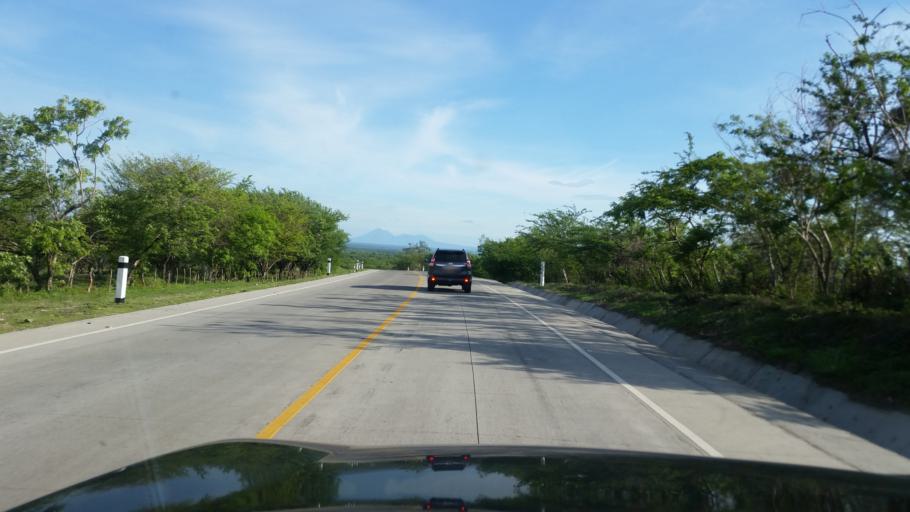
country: NI
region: Leon
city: Nagarote
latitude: 12.2092
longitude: -86.6812
